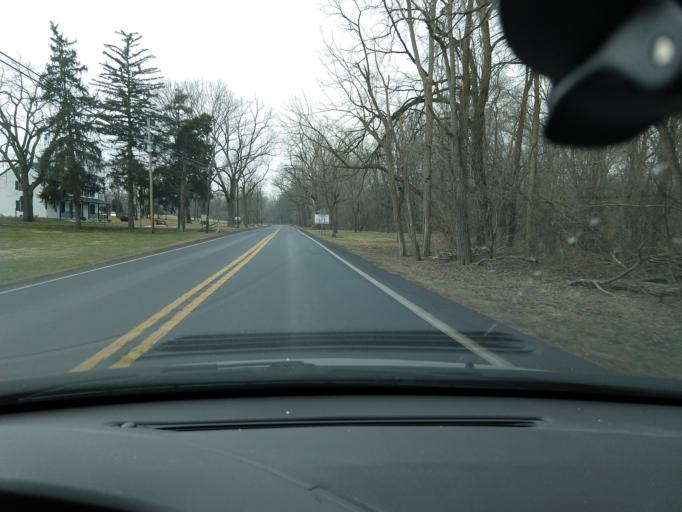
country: US
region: Pennsylvania
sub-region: Berks County
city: Amity Gardens
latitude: 40.2574
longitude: -75.7515
